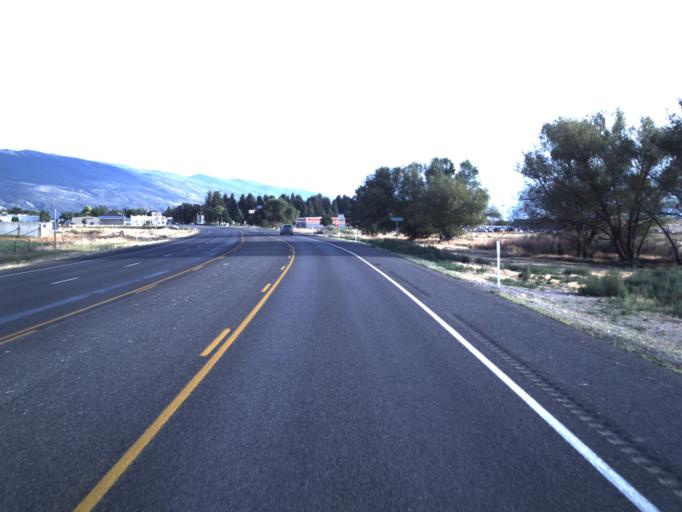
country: US
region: Utah
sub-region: Sanpete County
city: Ephraim
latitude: 39.3782
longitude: -111.5866
